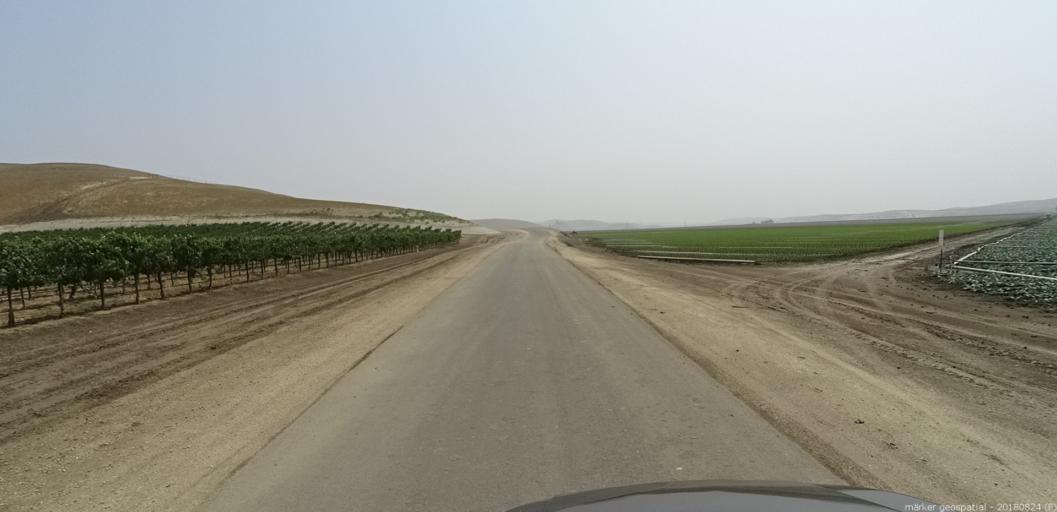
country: US
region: California
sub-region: Monterey County
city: King City
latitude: 36.1908
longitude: -121.0517
